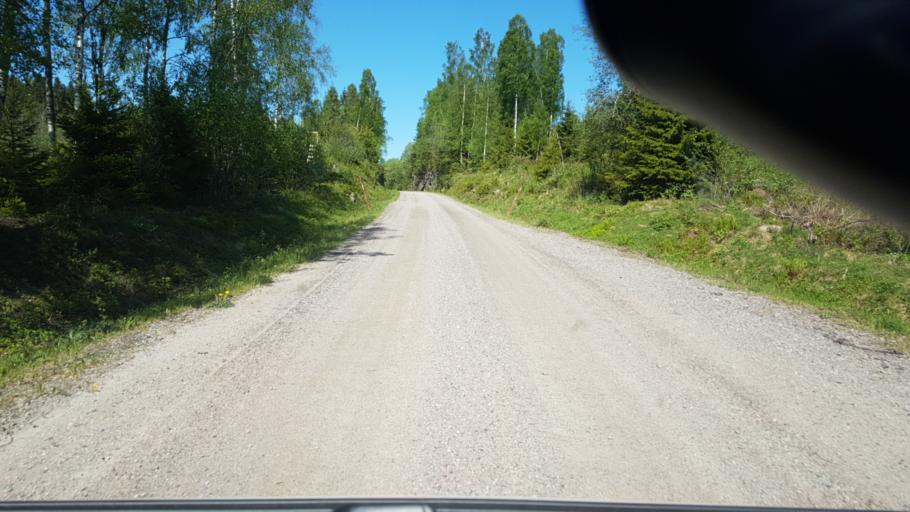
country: SE
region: Vaermland
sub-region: Eda Kommun
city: Charlottenberg
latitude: 59.9964
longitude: 12.5084
